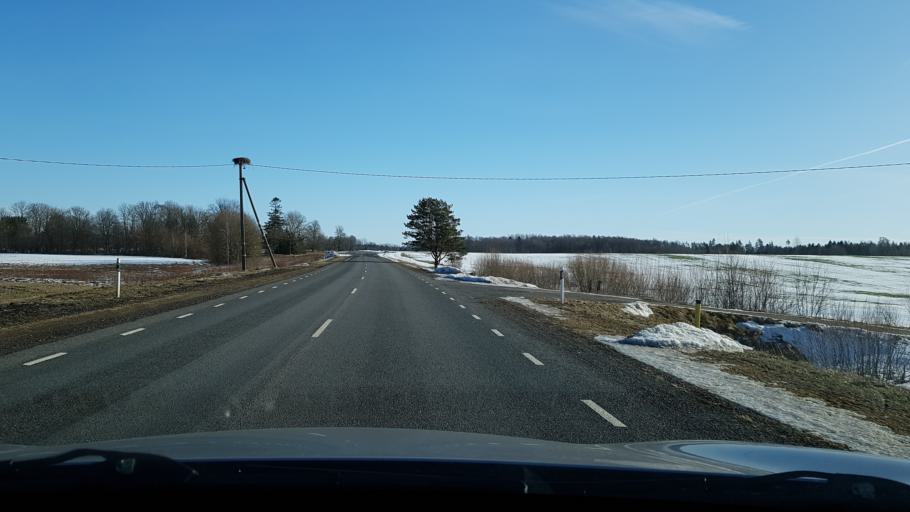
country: EE
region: Viljandimaa
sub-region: Suure-Jaani vald
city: Suure-Jaani
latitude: 58.5639
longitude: 25.4111
